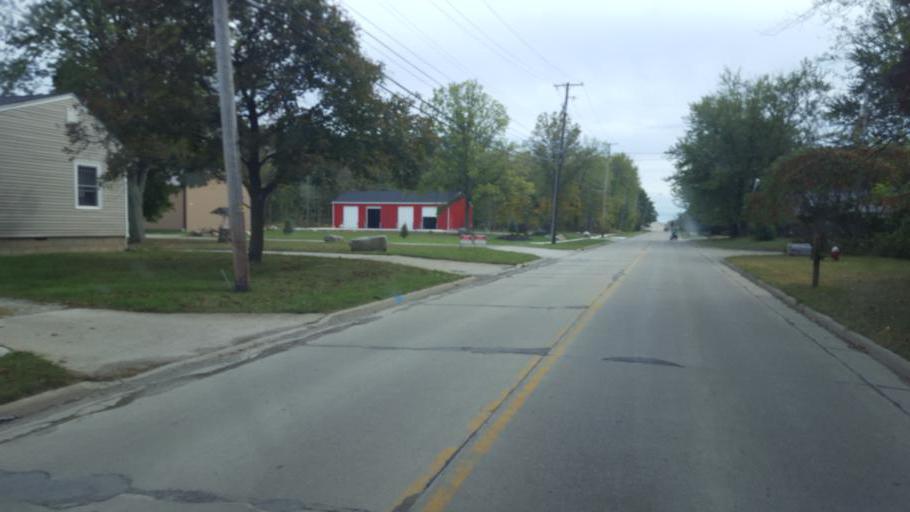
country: US
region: Ohio
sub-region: Lorain County
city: Sheffield Lake
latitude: 41.4924
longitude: -82.0757
